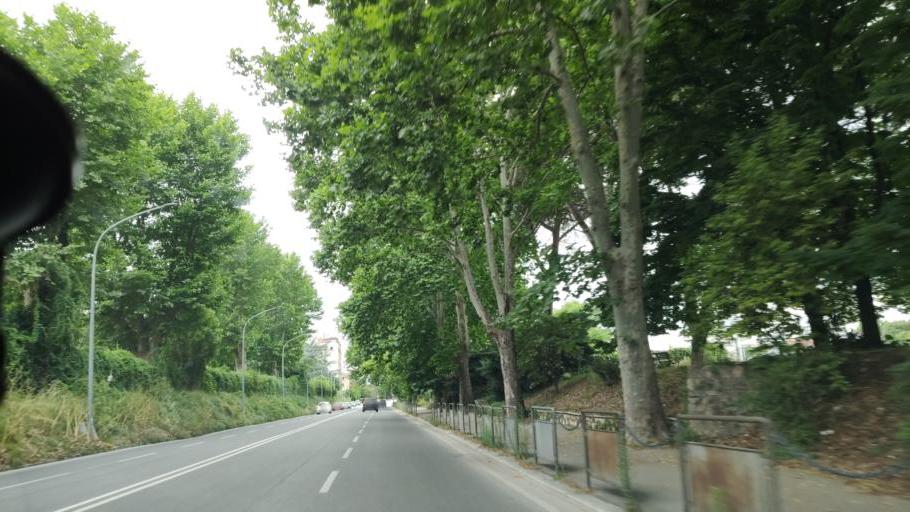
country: IT
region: Umbria
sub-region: Provincia di Terni
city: Terni
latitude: 42.5698
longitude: 12.6484
